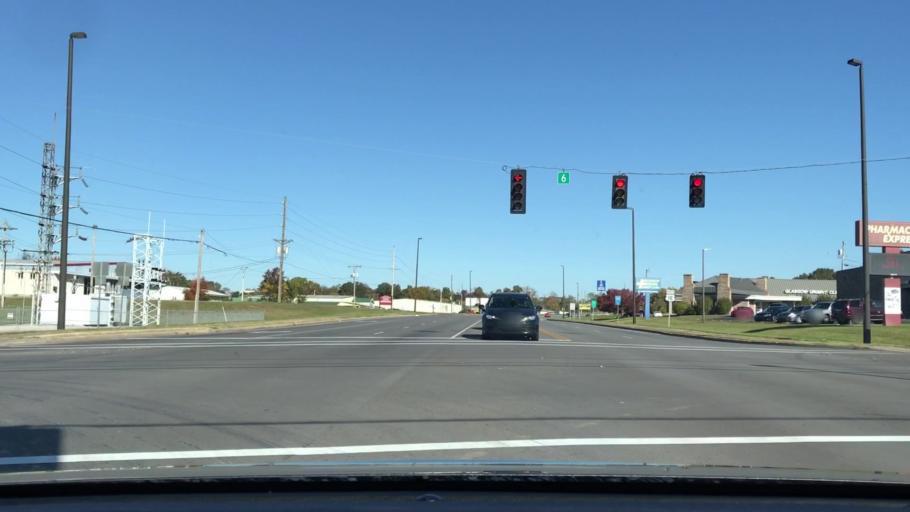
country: US
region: Kentucky
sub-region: Barren County
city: Glasgow
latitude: 36.9892
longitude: -85.9322
